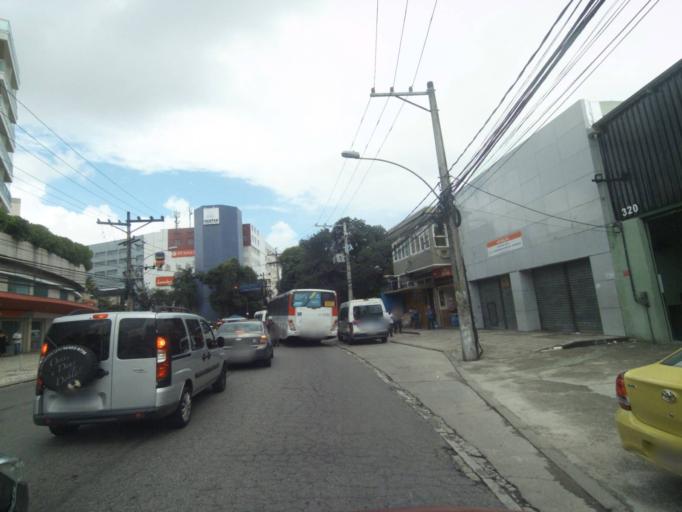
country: BR
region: Rio de Janeiro
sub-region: Sao Joao De Meriti
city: Sao Joao de Meriti
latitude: -22.9236
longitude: -43.3615
